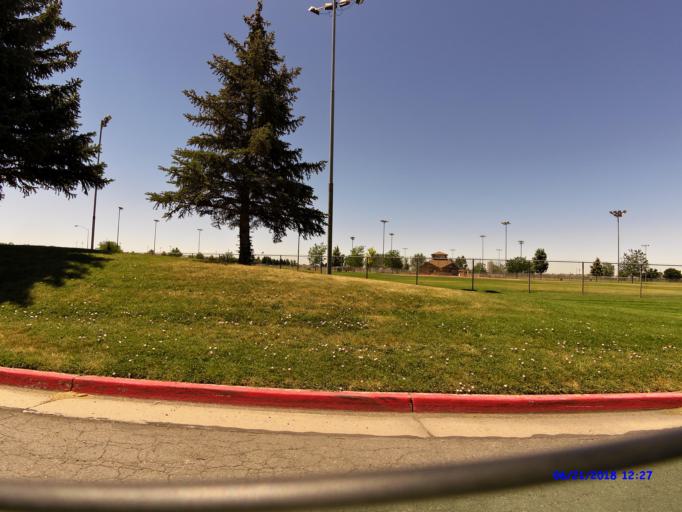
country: US
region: Utah
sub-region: Weber County
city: Harrisville
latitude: 41.2818
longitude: -111.9976
